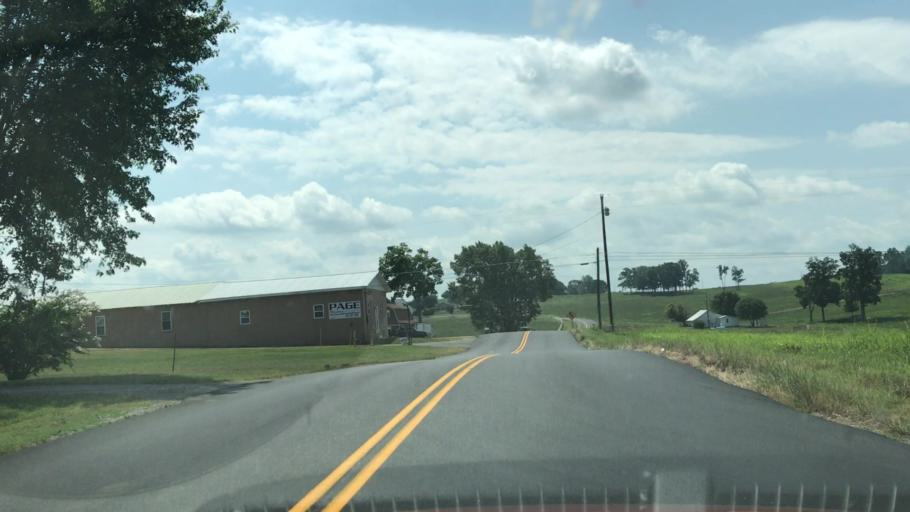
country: US
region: Kentucky
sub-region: Monroe County
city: Tompkinsville
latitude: 36.7323
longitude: -85.7311
